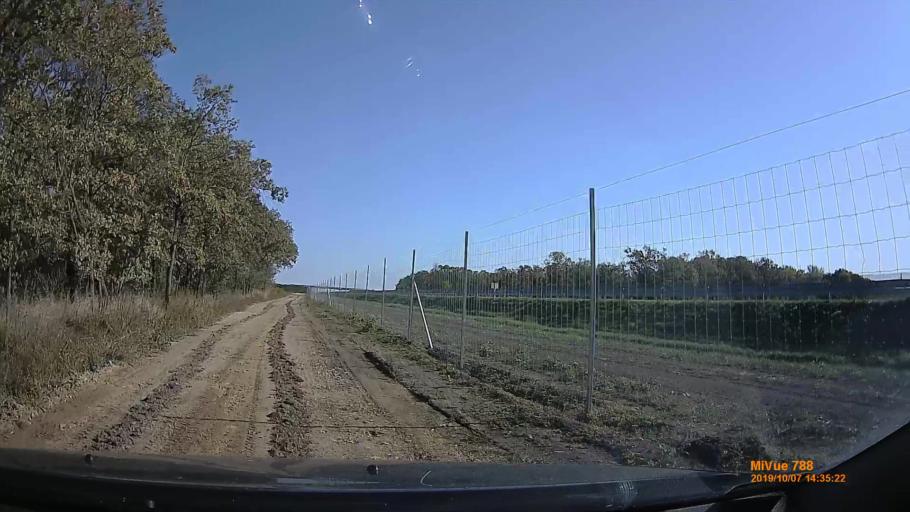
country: HU
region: Jasz-Nagykun-Szolnok
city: Kunszentmarton
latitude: 46.8580
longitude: 20.3082
